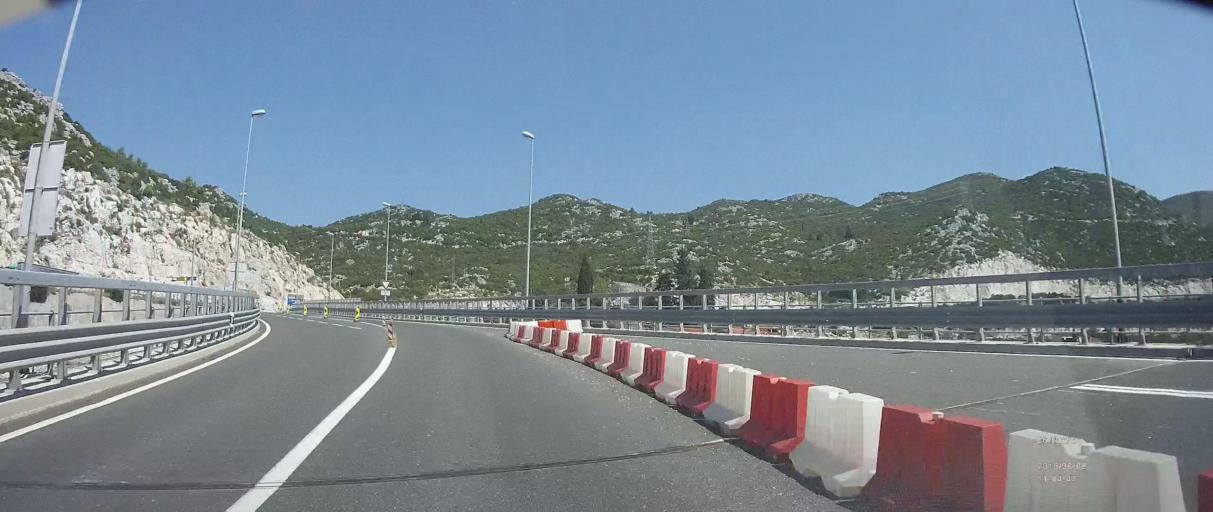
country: HR
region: Dubrovacko-Neretvanska
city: Komin
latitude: 43.0517
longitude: 17.4620
